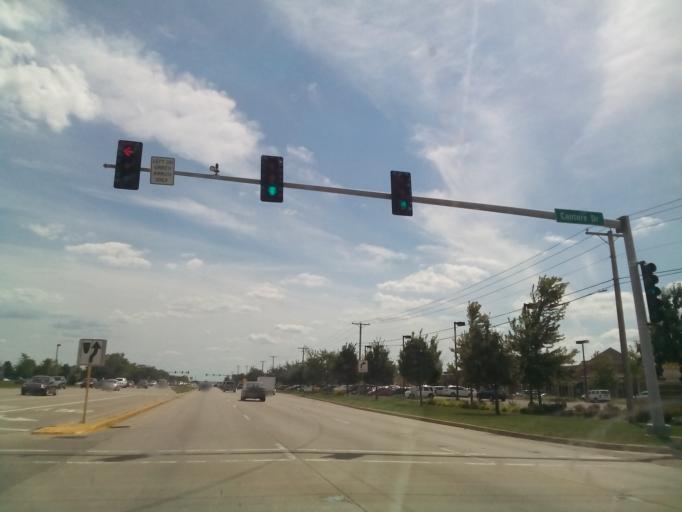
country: US
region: Illinois
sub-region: Will County
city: Plainfield
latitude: 41.7129
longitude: -88.2060
